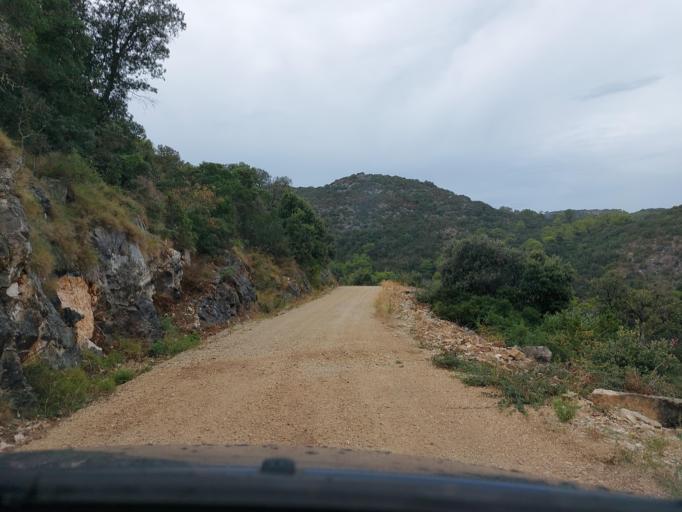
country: HR
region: Dubrovacko-Neretvanska
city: Smokvica
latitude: 42.7484
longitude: 16.9155
